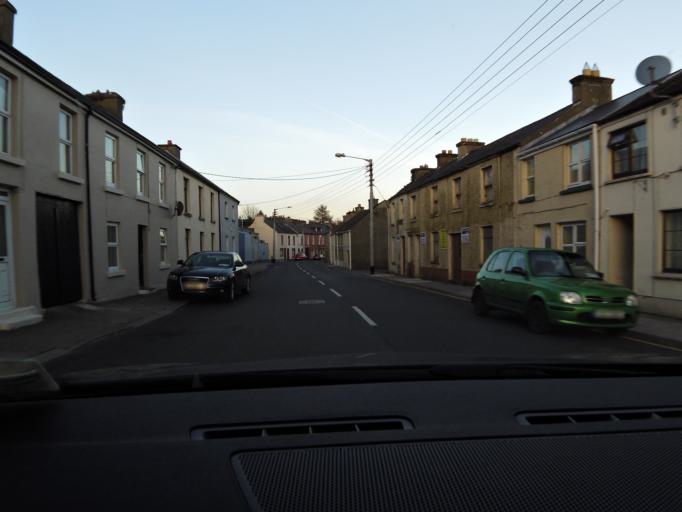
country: IE
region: Connaught
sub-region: Roscommon
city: Boyle
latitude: 53.9730
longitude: -8.3076
